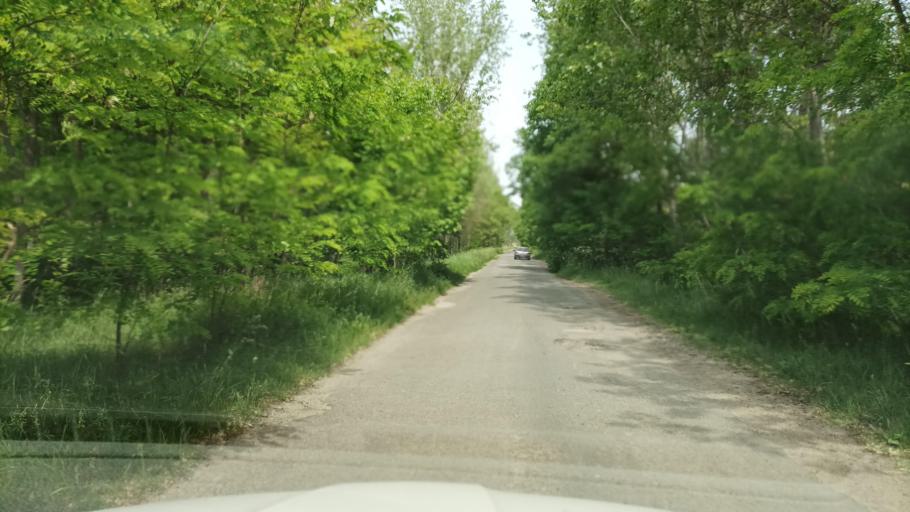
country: HU
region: Fejer
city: Racalmas
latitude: 47.0793
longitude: 18.9400
